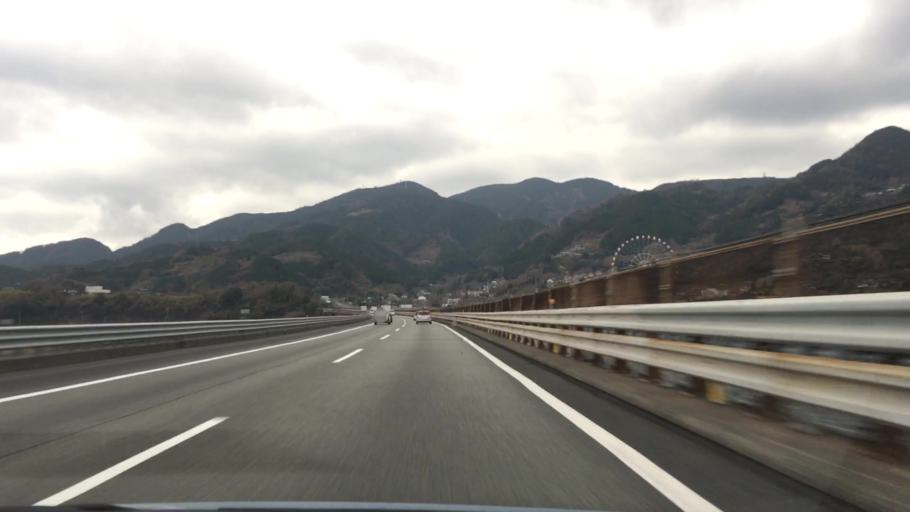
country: JP
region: Shizuoka
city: Fujinomiya
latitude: 35.1639
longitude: 138.6253
